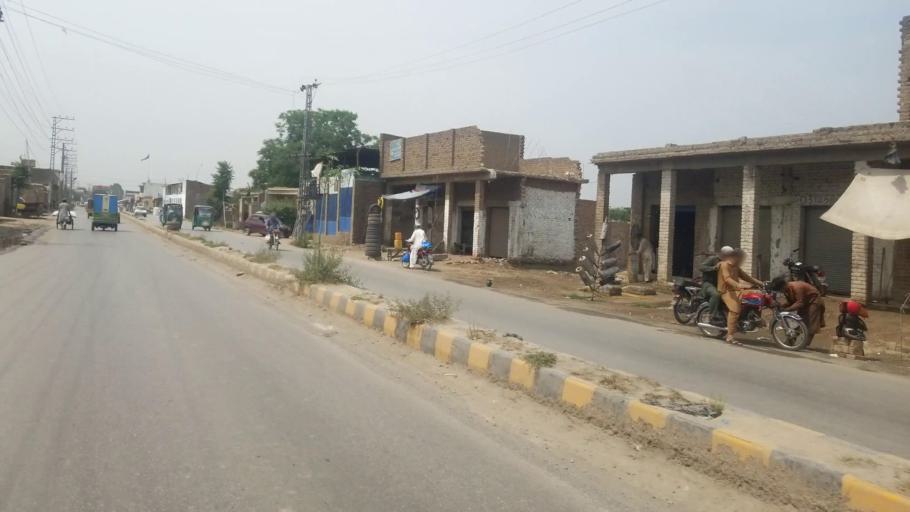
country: PK
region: Khyber Pakhtunkhwa
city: Peshawar
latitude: 33.9947
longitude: 71.6111
